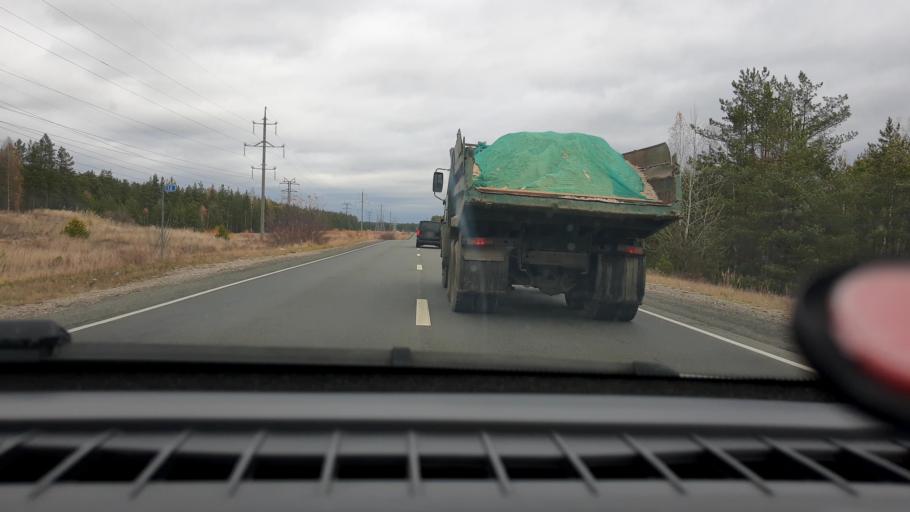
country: RU
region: Nizjnij Novgorod
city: Lukino
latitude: 56.3928
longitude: 43.6443
